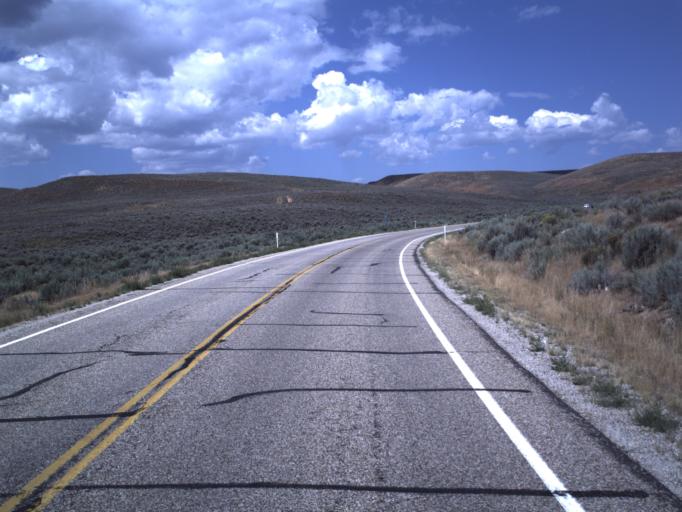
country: US
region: Utah
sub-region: Rich County
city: Randolph
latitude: 41.7690
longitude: -111.1721
